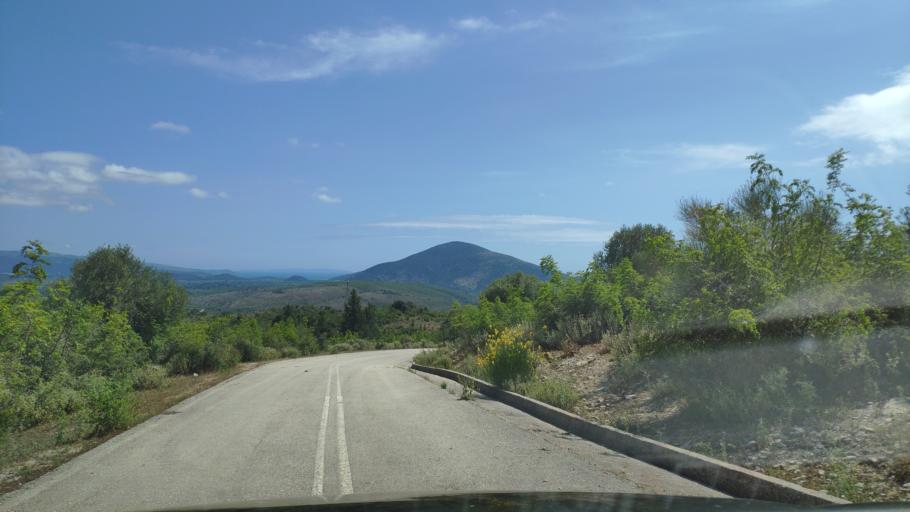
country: AL
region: Vlore
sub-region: Rrethi i Sarandes
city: Konispol
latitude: 39.6315
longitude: 20.2119
